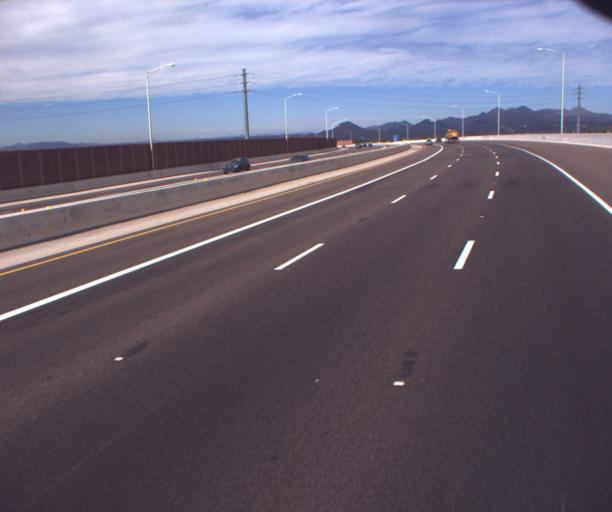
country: US
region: Arizona
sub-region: Pinal County
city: Apache Junction
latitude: 33.4712
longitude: -111.6823
